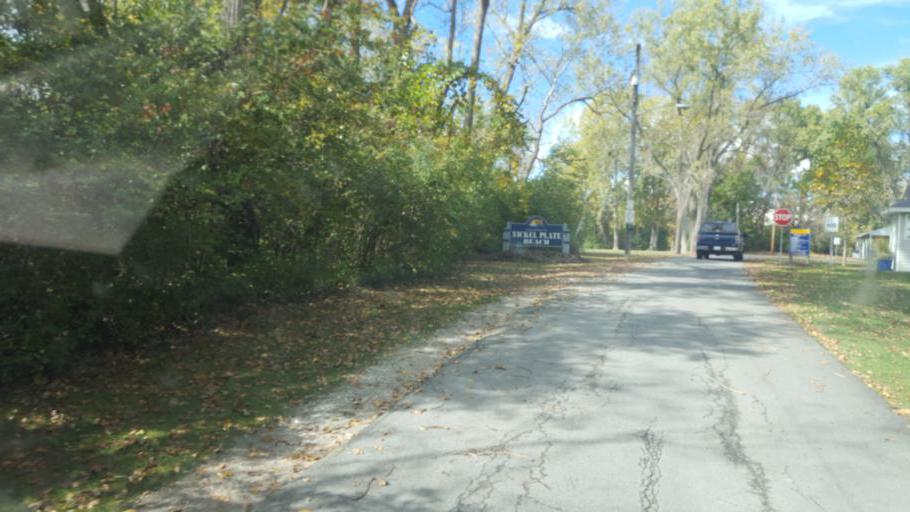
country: US
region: Ohio
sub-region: Erie County
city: Huron
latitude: 41.3945
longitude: -82.5444
